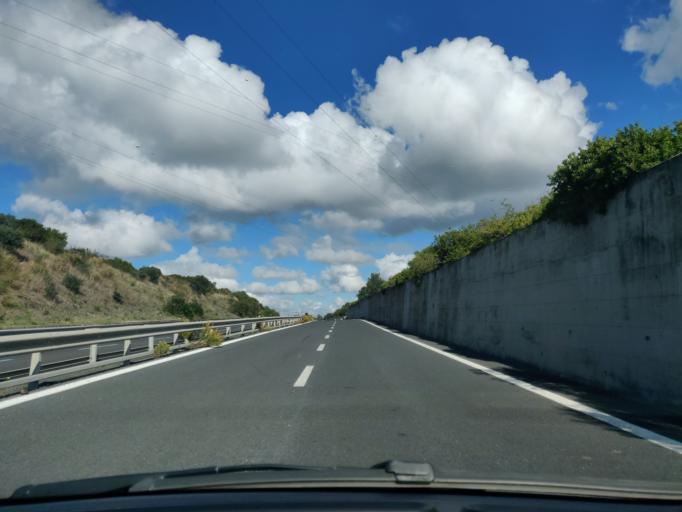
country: IT
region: Latium
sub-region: Citta metropolitana di Roma Capitale
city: Civitavecchia
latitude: 42.1129
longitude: 11.7925
